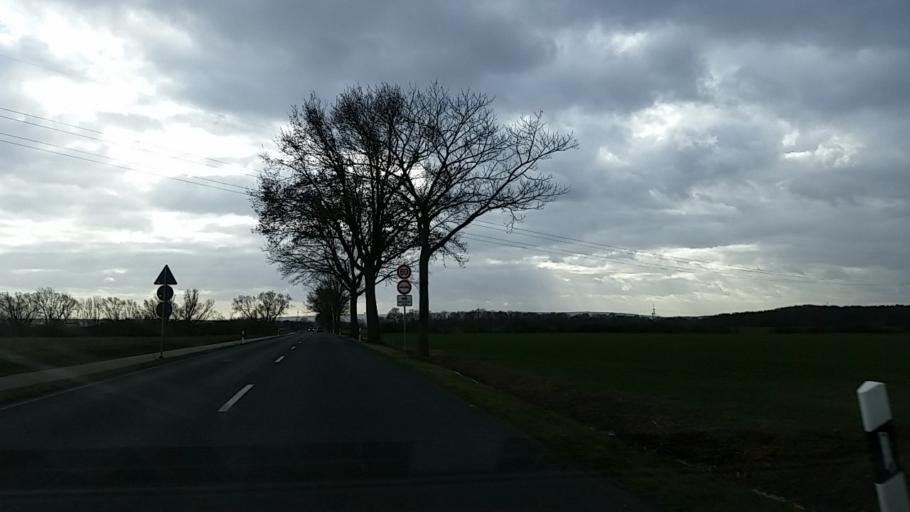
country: DE
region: Lower Saxony
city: Gross Twulpstedt
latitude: 52.3548
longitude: 10.8552
